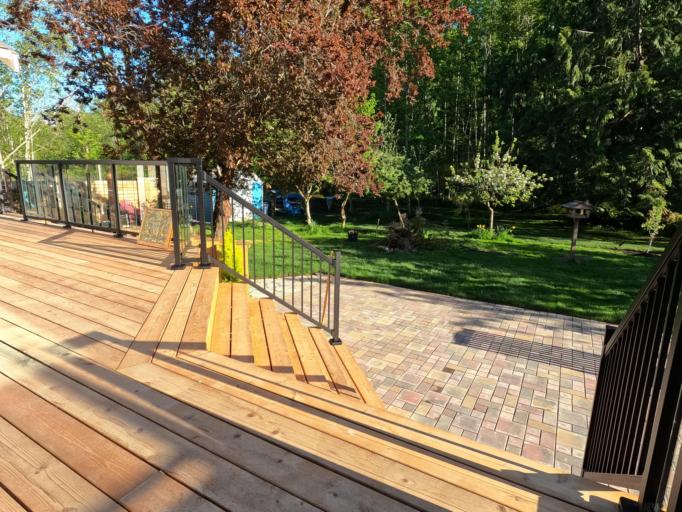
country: CA
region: British Columbia
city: Nanaimo
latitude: 49.1707
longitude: -123.7782
